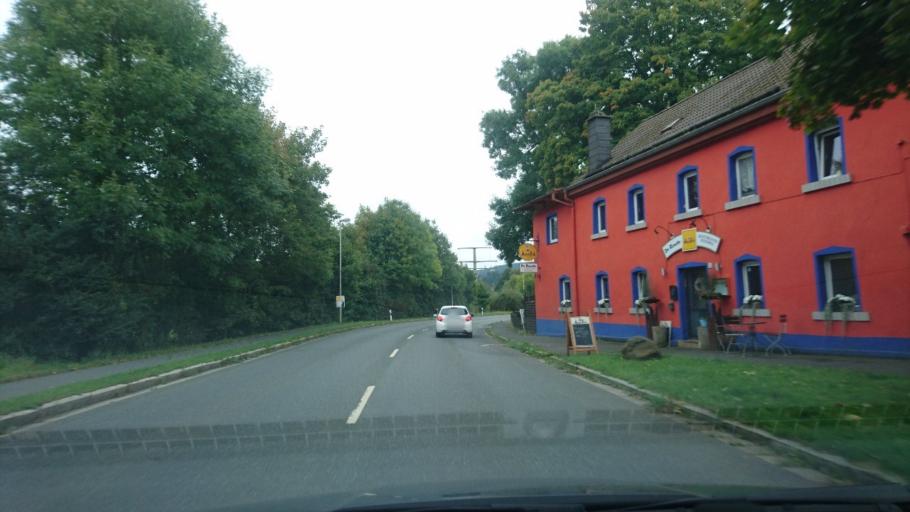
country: DE
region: Bavaria
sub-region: Upper Franconia
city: Naila
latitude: 50.3554
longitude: 11.6898
